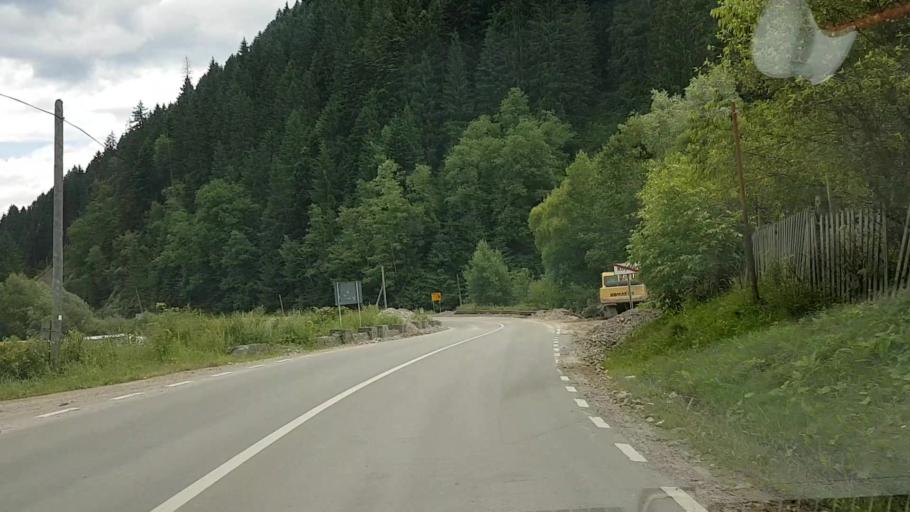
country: RO
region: Neamt
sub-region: Comuna Poiana Teiului
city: Poiana Teiului
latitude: 47.0940
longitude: 25.9457
